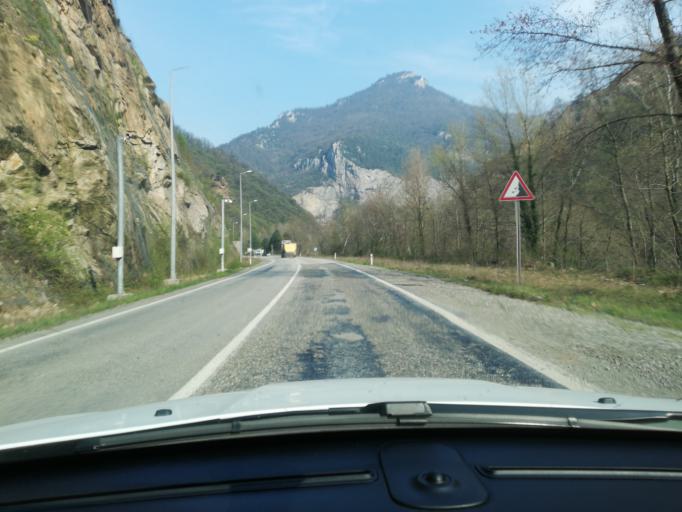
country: TR
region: Karabuk
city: Yenice
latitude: 41.1845
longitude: 32.4464
